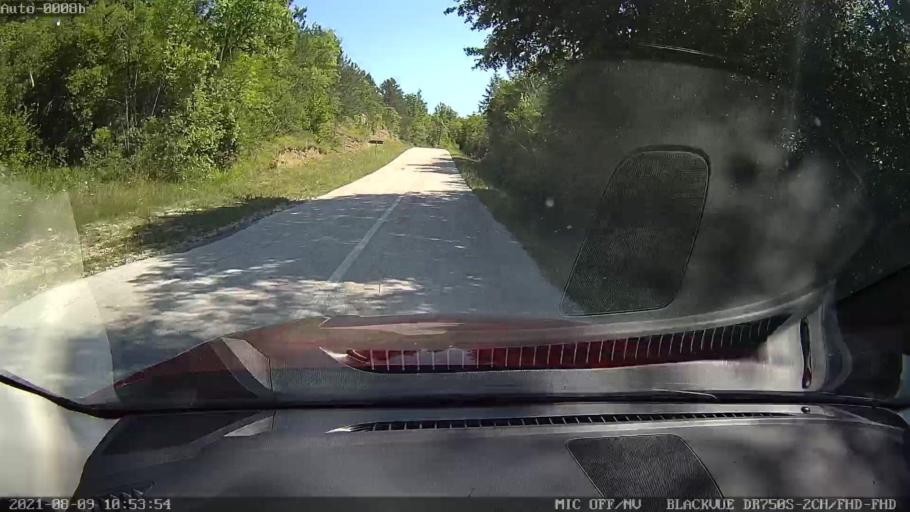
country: HR
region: Istarska
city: Pazin
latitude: 45.2777
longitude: 14.0709
